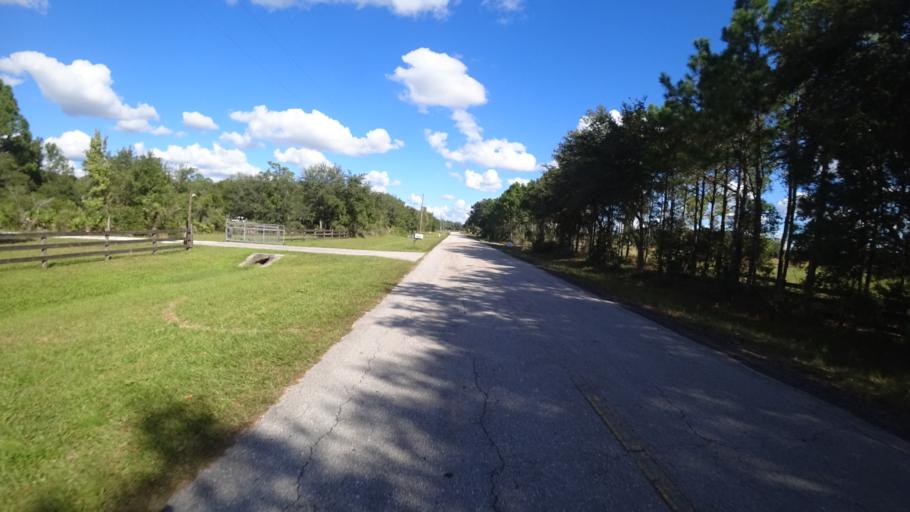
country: US
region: Florida
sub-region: Sarasota County
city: Warm Mineral Springs
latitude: 27.2741
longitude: -82.1223
